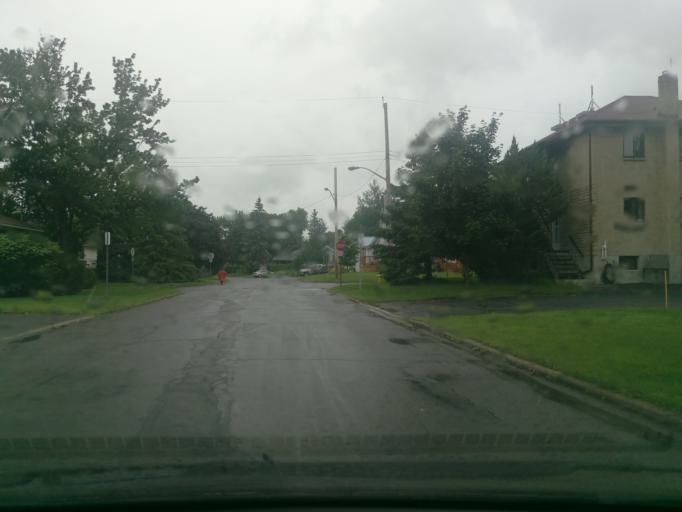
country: CA
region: Ontario
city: Ottawa
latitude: 45.4335
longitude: -75.6454
